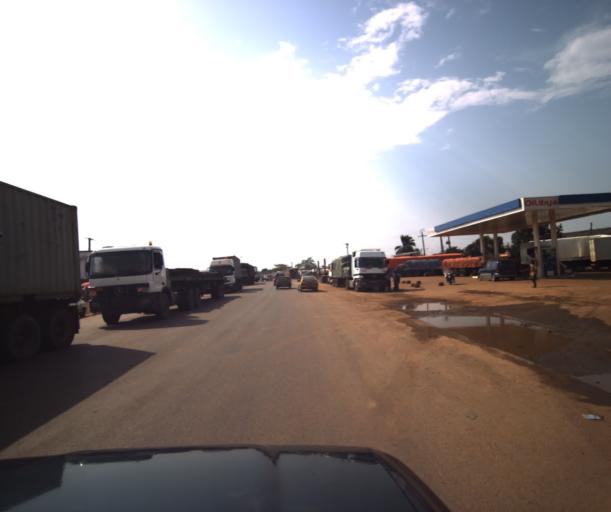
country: CM
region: Littoral
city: Douala
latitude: 4.0174
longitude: 9.7256
